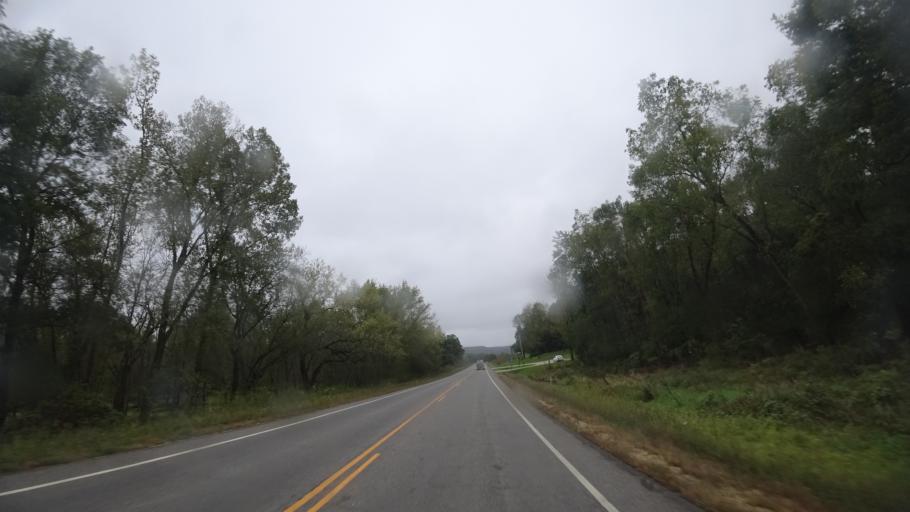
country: US
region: Wisconsin
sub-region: Crawford County
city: Prairie du Chien
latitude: 43.0399
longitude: -90.9875
